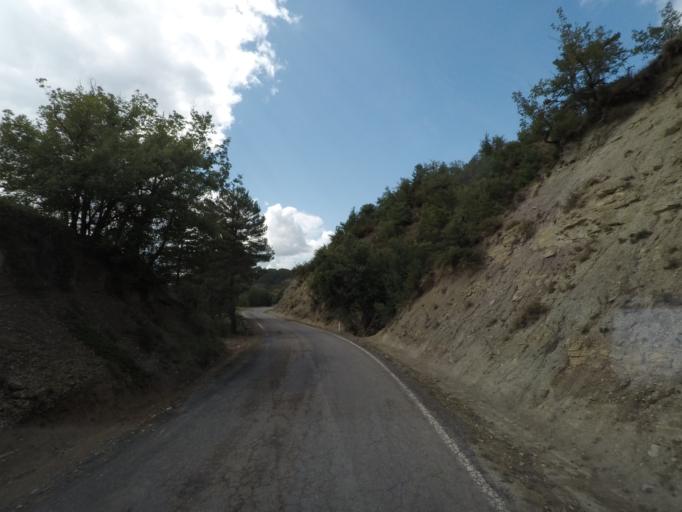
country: ES
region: Aragon
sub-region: Provincia de Huesca
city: Yebra de Basa
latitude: 42.4012
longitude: -0.2545
